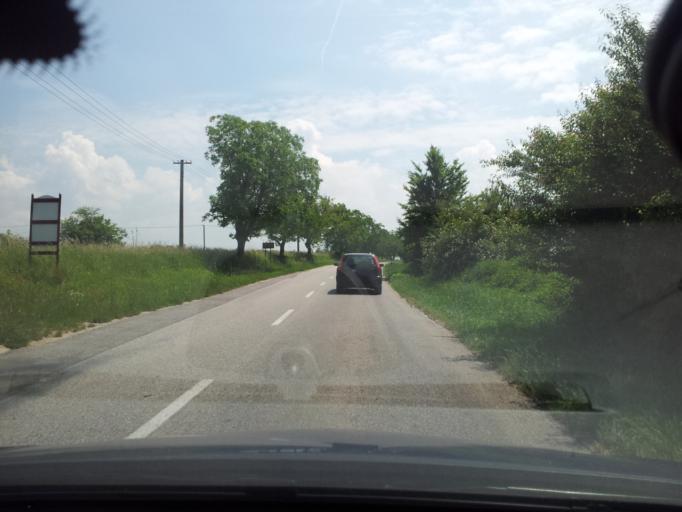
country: SK
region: Nitriansky
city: Zlate Moravce
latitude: 48.3789
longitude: 18.4064
